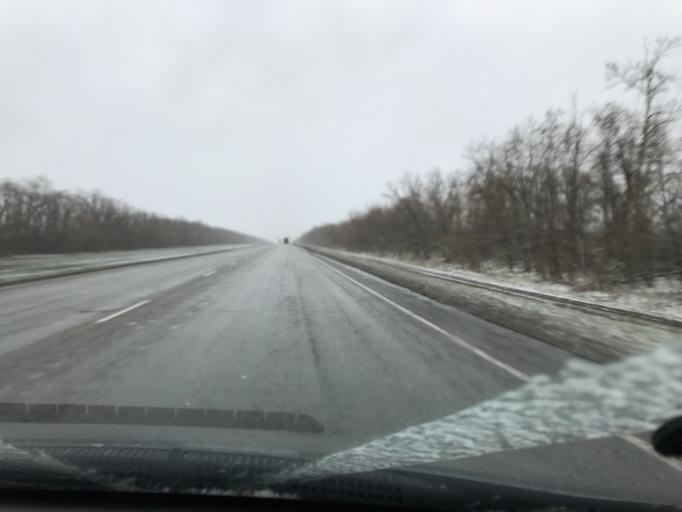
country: RU
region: Rostov
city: Mechetinskaya
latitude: 46.7438
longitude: 40.4676
